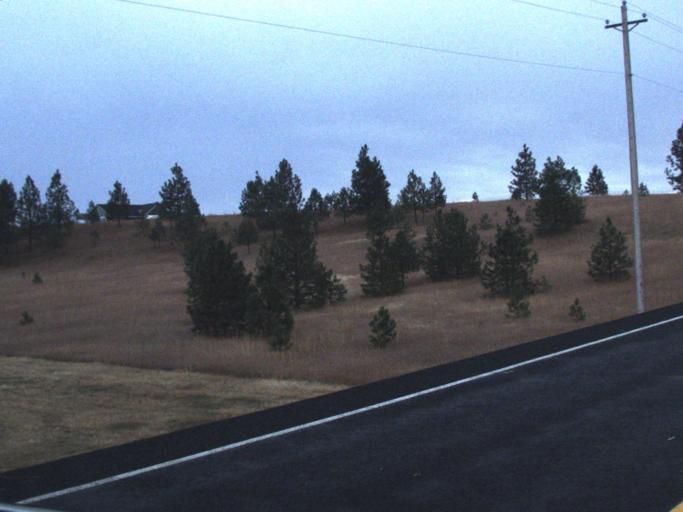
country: US
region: Washington
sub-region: Lincoln County
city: Davenport
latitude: 47.7850
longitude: -118.1736
